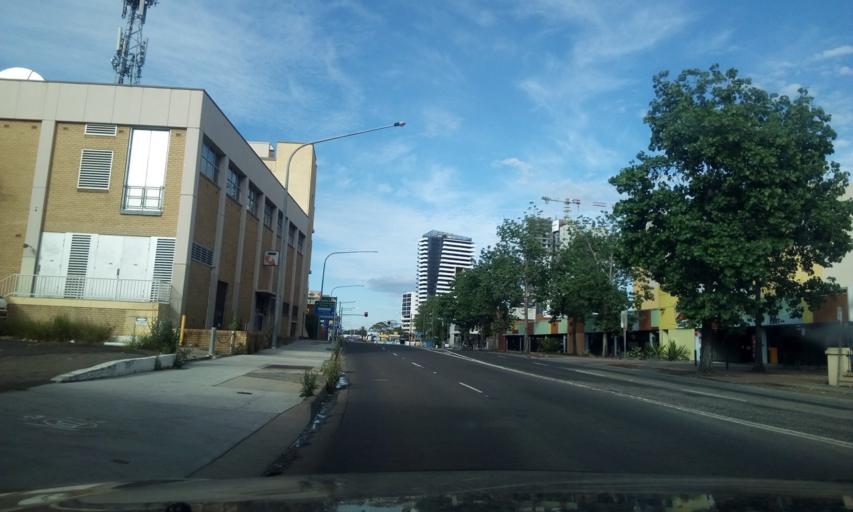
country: AU
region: New South Wales
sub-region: Fairfield
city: Liverpool
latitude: -33.9256
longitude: 150.9245
